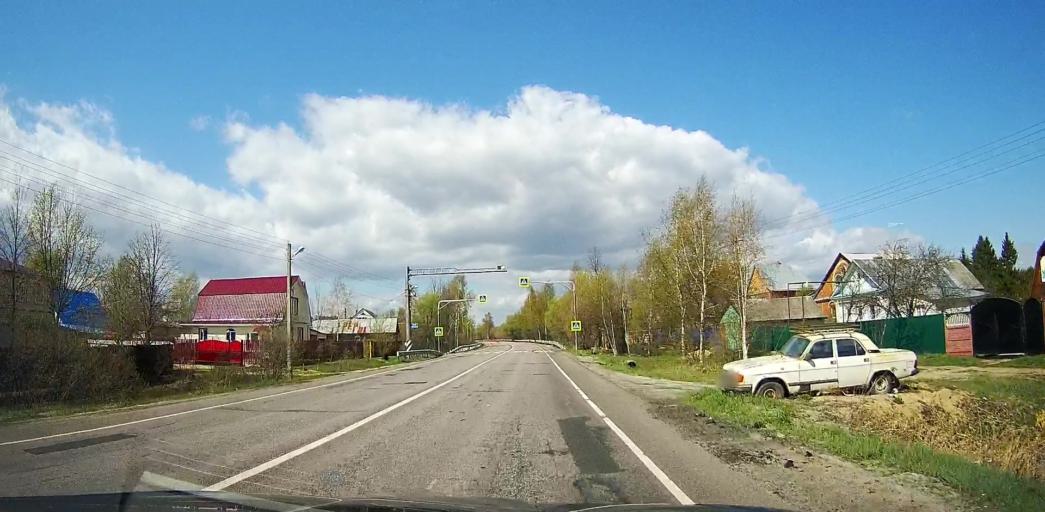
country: RU
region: Moskovskaya
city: Imeni Tsyurupy
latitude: 55.5354
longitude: 38.6684
